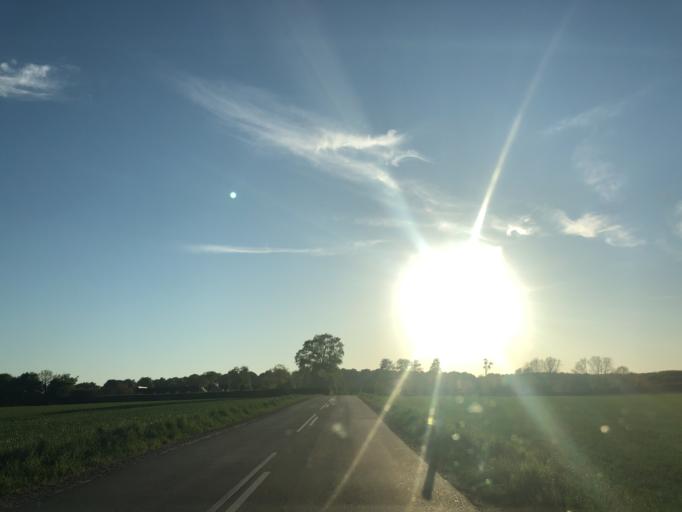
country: DK
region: Zealand
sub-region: Koge Kommune
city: Bjaeverskov
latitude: 55.4241
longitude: 12.0879
